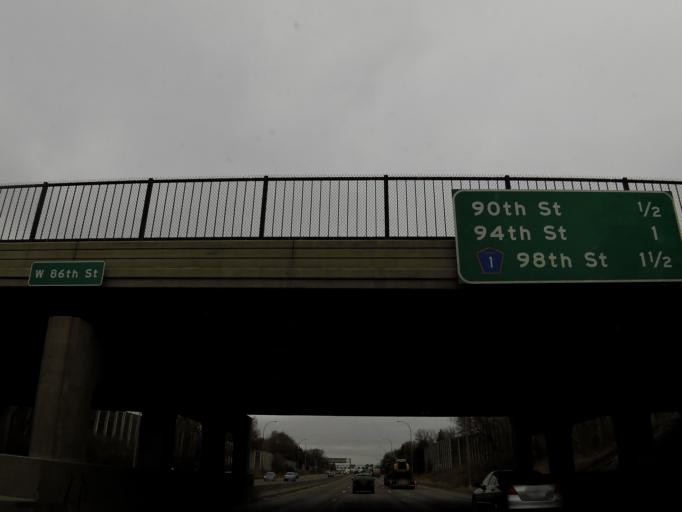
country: US
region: Minnesota
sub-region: Hennepin County
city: Bloomington
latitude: 44.8483
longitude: -93.2983
